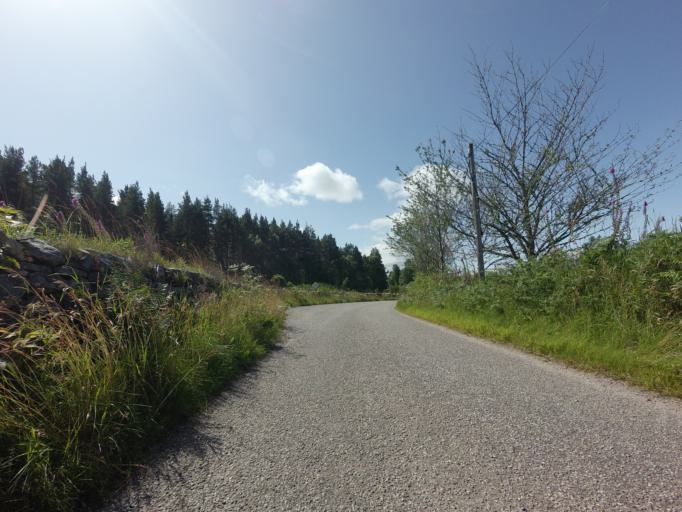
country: GB
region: Scotland
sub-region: Highland
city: Nairn
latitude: 57.5007
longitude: -3.9395
